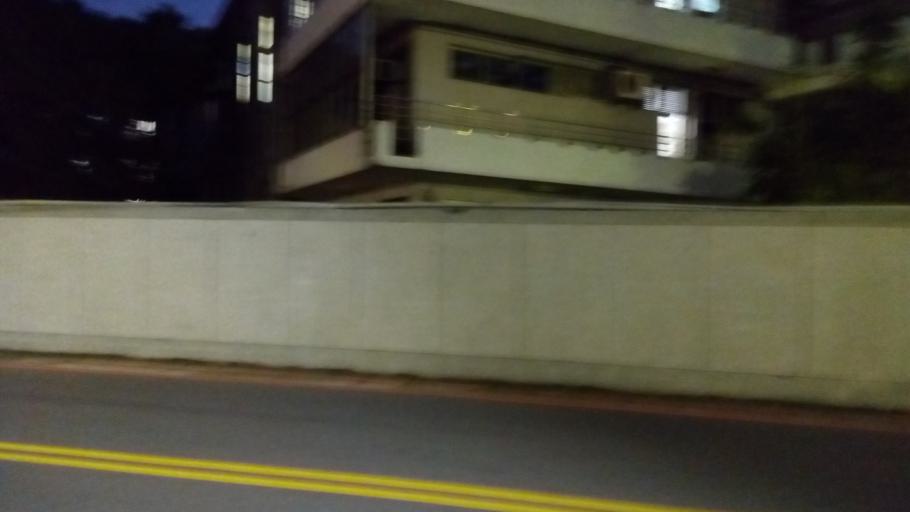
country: TW
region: Taipei
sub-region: Taipei
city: Banqiao
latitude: 25.0342
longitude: 121.4312
